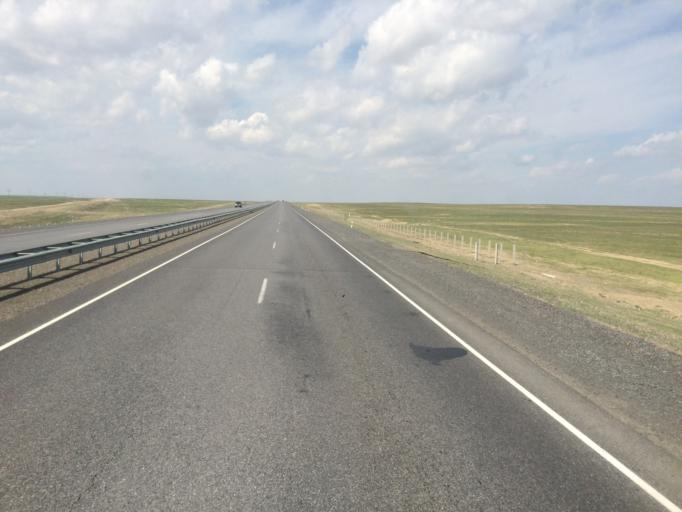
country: KZ
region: Qyzylorda
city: Shalqiya
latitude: 43.8577
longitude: 67.4022
